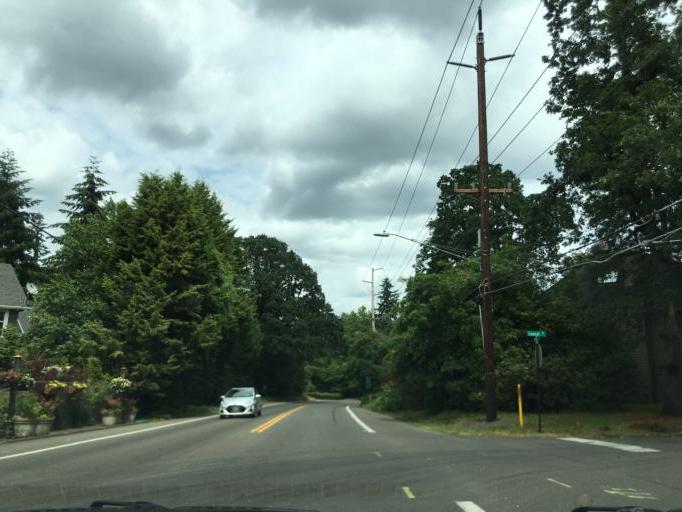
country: US
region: Oregon
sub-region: Clackamas County
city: Lake Oswego
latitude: 45.4077
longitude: -122.6756
